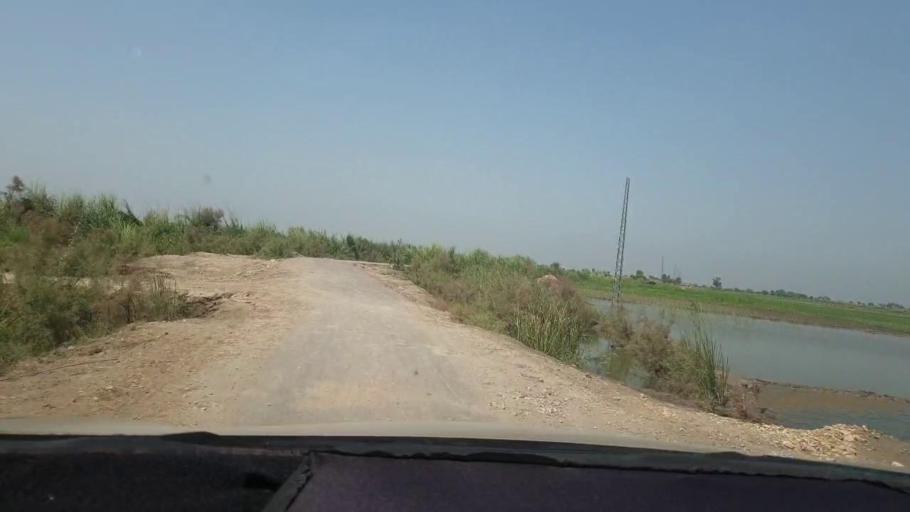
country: PK
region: Sindh
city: Shahdadkot
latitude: 27.8356
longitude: 67.8776
